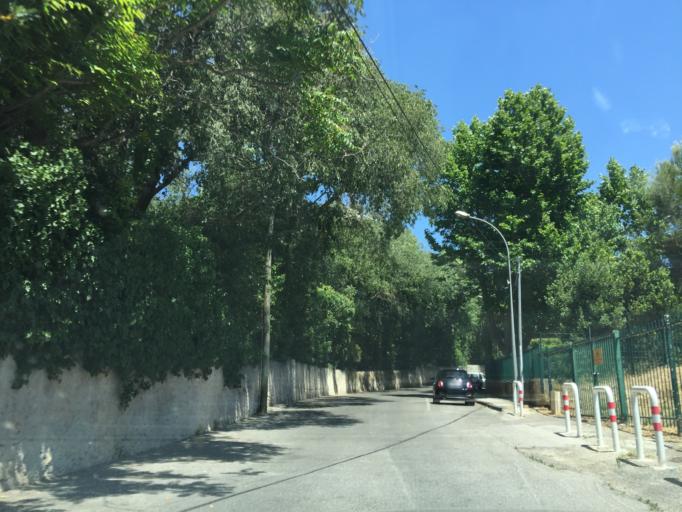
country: FR
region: Provence-Alpes-Cote d'Azur
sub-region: Departement des Bouches-du-Rhone
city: Marseille 09
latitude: 43.2514
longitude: 5.4082
